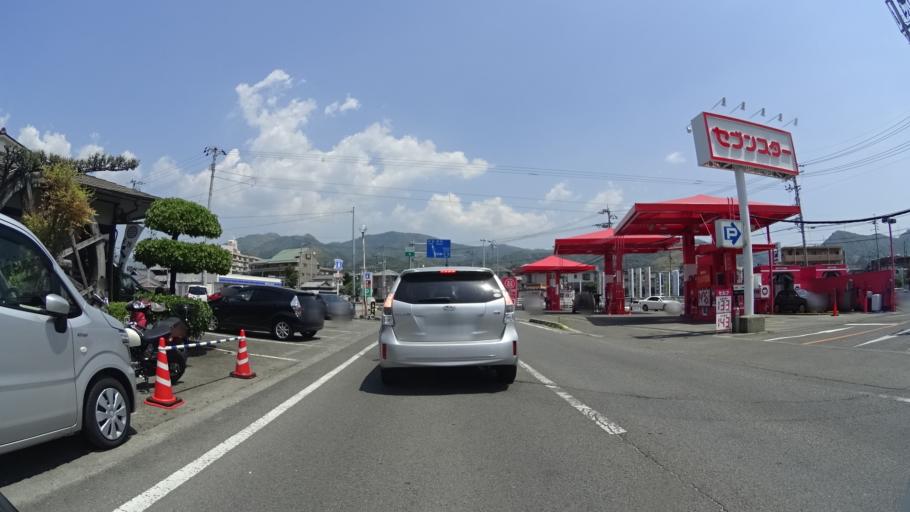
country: JP
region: Ehime
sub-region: Shikoku-chuo Shi
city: Matsuyama
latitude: 33.8491
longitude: 132.8009
